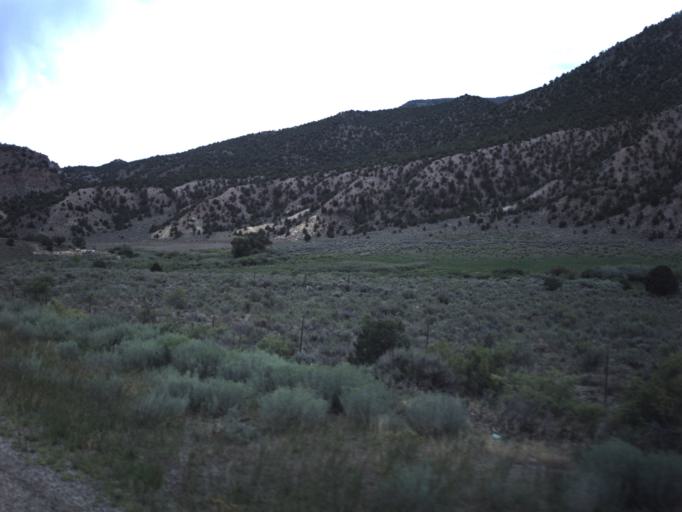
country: US
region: Utah
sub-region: Piute County
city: Junction
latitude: 38.1957
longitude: -112.1182
